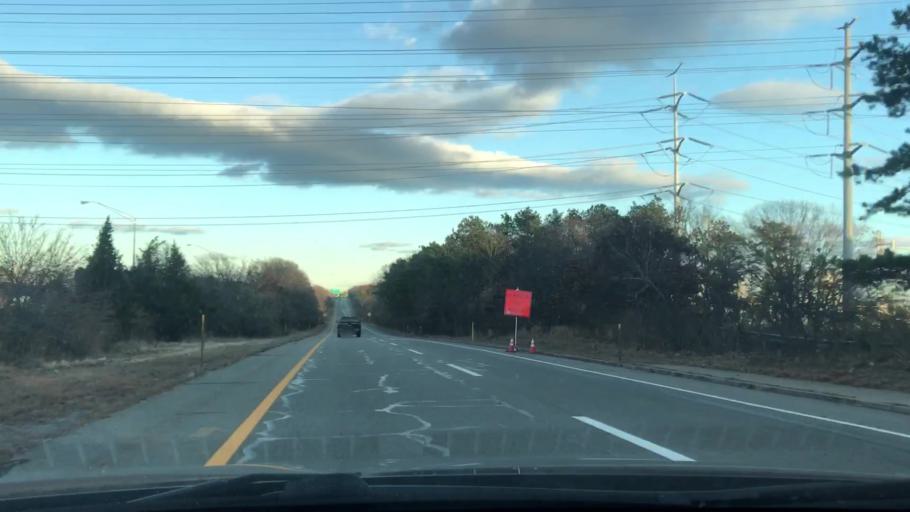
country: US
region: New York
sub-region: Suffolk County
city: Holbrook
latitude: 40.8168
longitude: -73.0719
